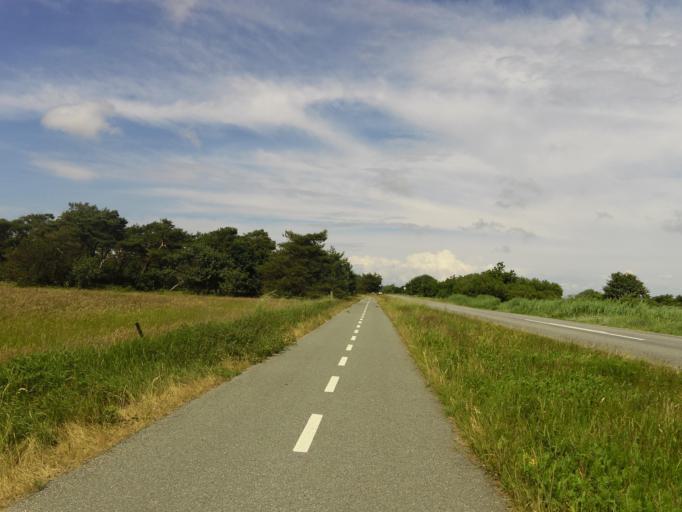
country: DE
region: Schleswig-Holstein
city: List
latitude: 55.1538
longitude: 8.5498
